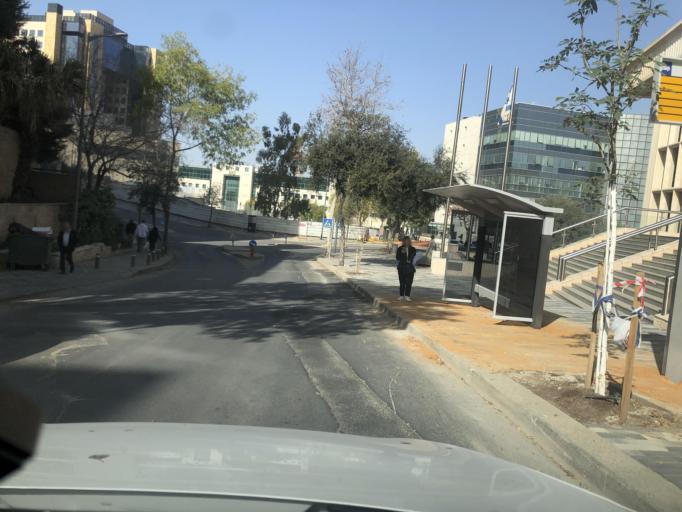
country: IL
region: Jerusalem
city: West Jerusalem
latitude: 31.8026
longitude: 35.2132
